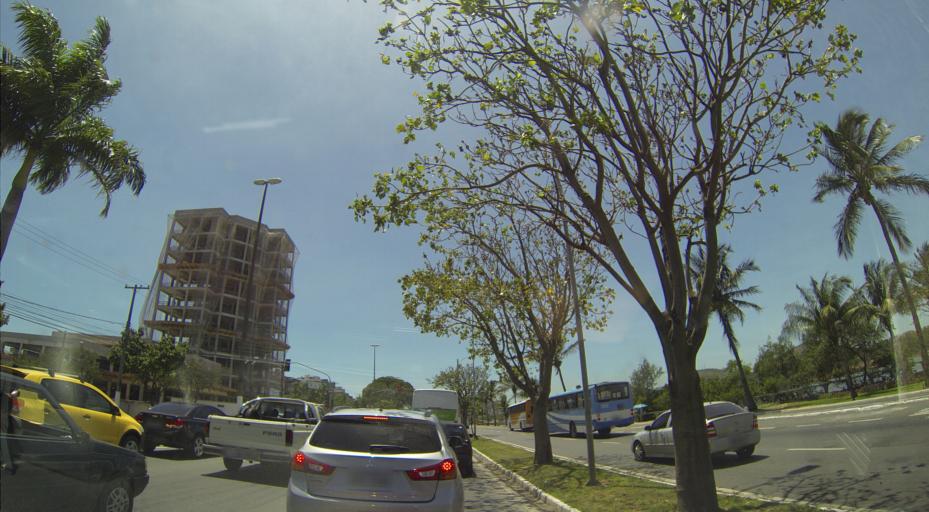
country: BR
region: Espirito Santo
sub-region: Vitoria
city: Vitoria
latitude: -20.3180
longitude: -40.3200
